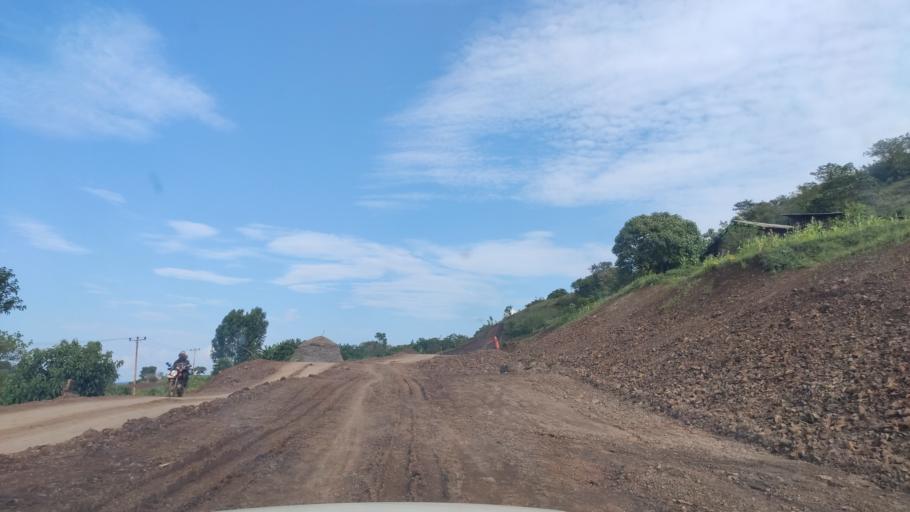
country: ET
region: Southern Nations, Nationalities, and People's Region
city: Arba Minch'
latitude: 6.4210
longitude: 37.3544
